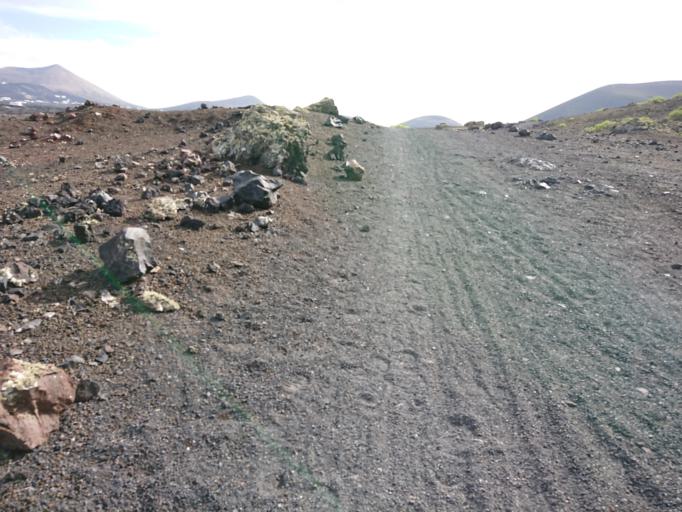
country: ES
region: Canary Islands
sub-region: Provincia de Las Palmas
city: Tias
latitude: 29.0072
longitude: -13.6756
